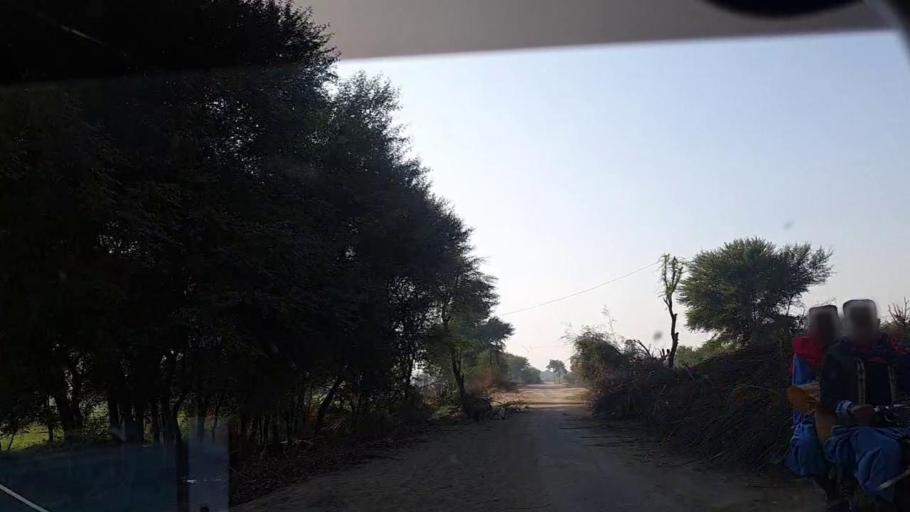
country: PK
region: Sindh
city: Sobhadero
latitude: 27.2336
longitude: 68.2704
